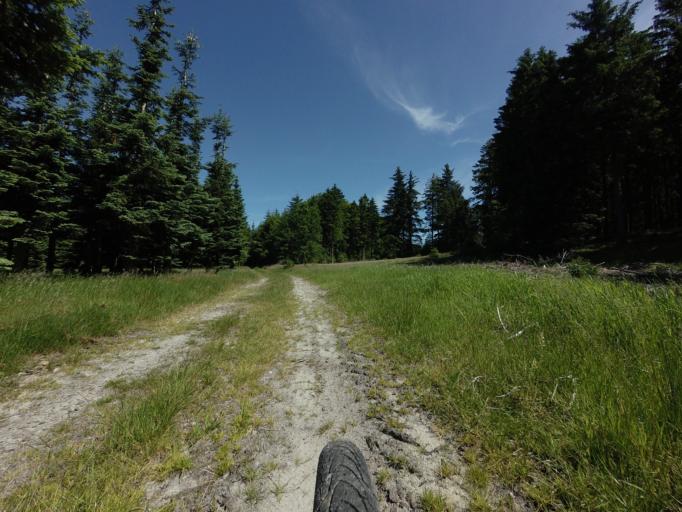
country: DK
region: Central Jutland
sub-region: Silkeborg Kommune
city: Virklund
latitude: 56.0574
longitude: 9.4735
